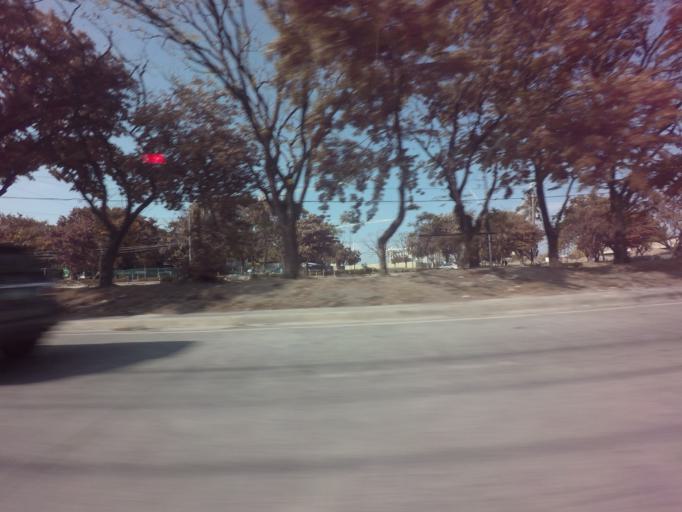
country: PH
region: Calabarzon
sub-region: Province of Rizal
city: Taguig
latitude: 14.5019
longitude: 121.0438
